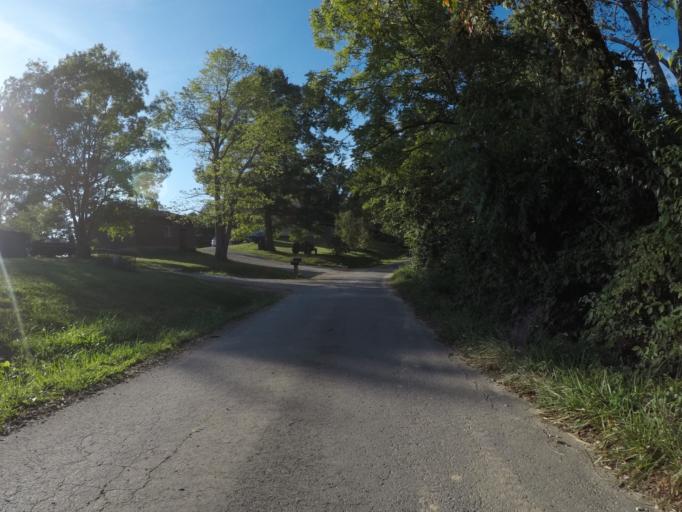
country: US
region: Ohio
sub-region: Lawrence County
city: Coal Grove
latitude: 38.5847
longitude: -82.5494
